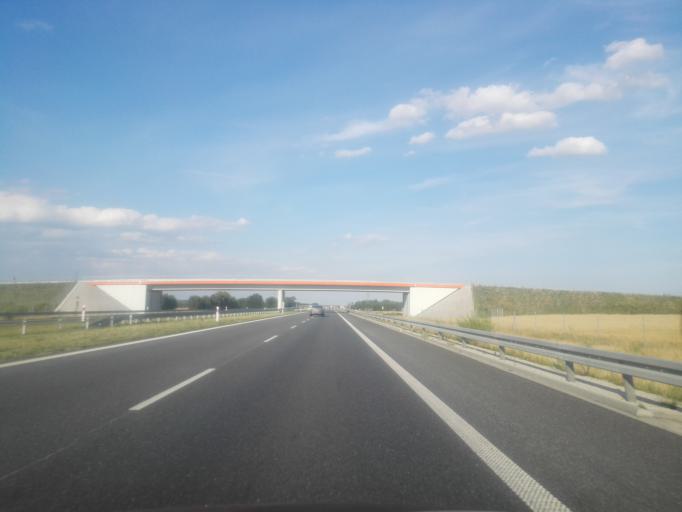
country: PL
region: Greater Poland Voivodeship
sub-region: Powiat kepinski
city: Bralin
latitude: 51.3118
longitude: 17.9419
